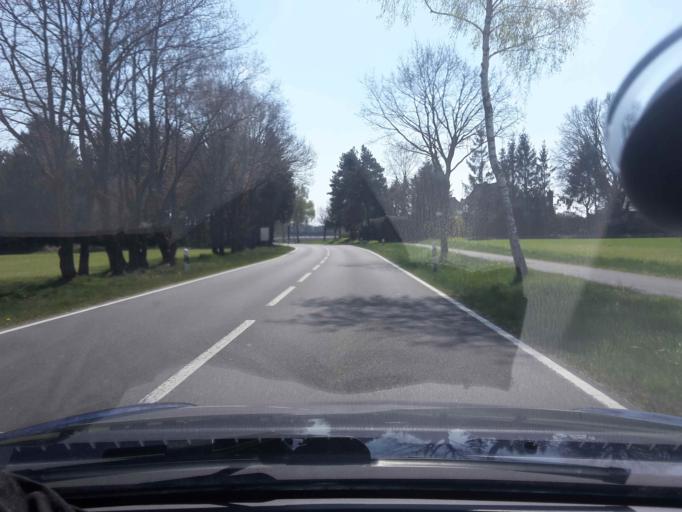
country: DE
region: Lower Saxony
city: Schneverdingen
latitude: 53.0888
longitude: 9.8477
